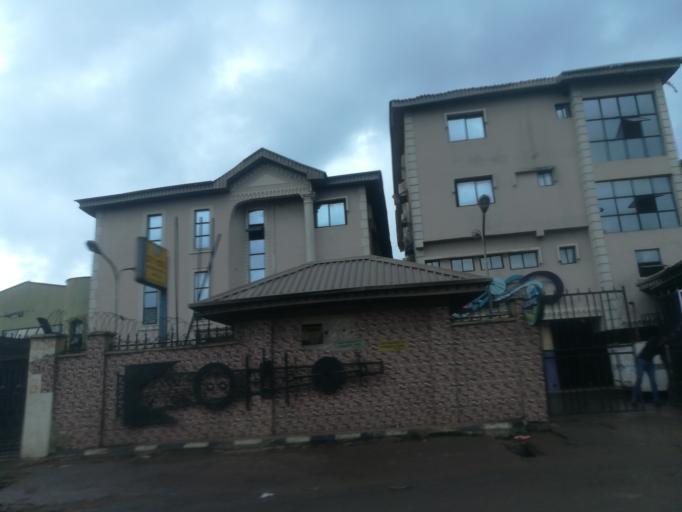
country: NG
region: Lagos
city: Agege
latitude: 6.6258
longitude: 3.3123
